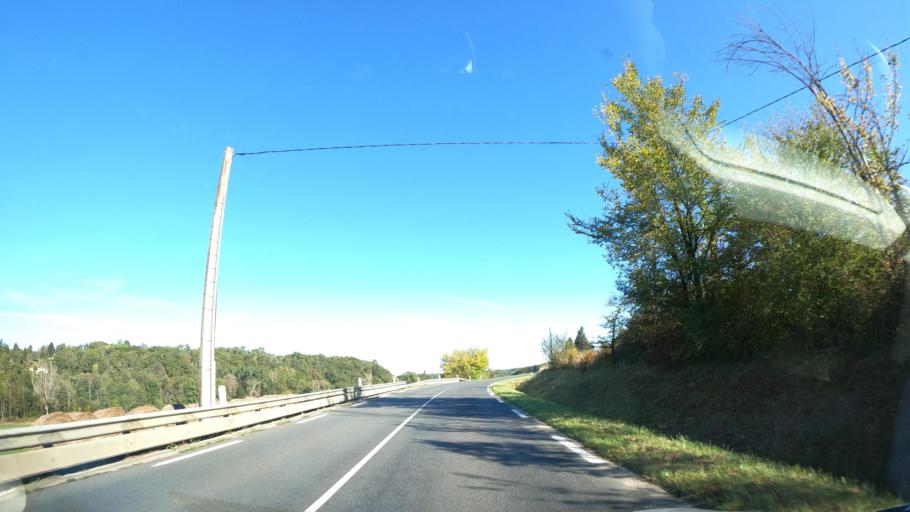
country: FR
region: Aquitaine
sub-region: Departement de la Dordogne
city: Lembras
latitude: 44.9105
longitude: 0.5576
